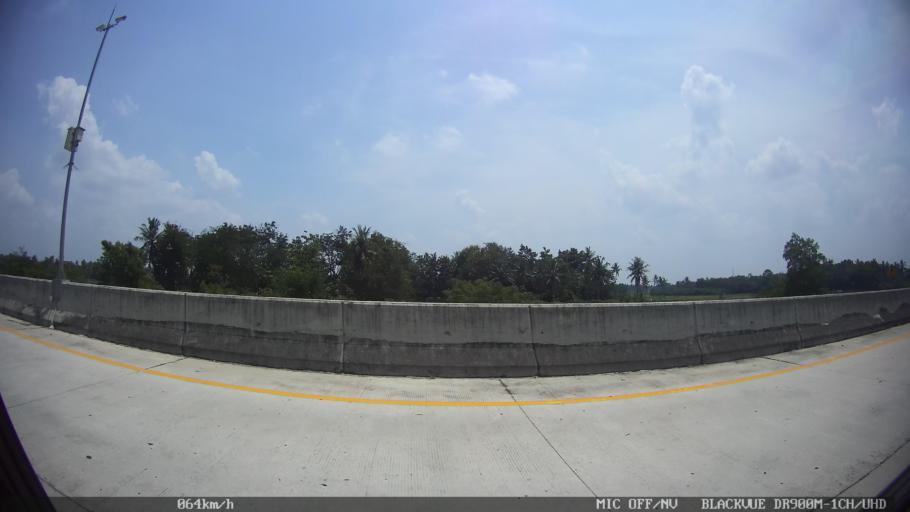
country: ID
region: Lampung
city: Natar
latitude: -5.2923
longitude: 105.2319
